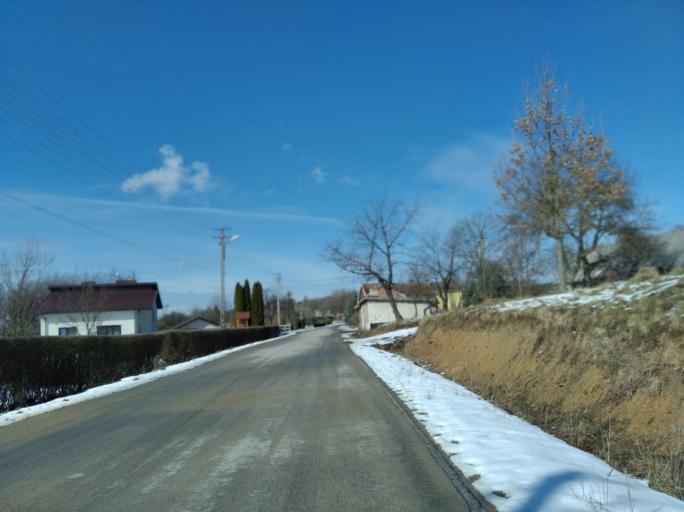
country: PL
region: Subcarpathian Voivodeship
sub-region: Powiat brzozowski
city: Jablonica Polska
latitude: 49.7238
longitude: 21.8792
